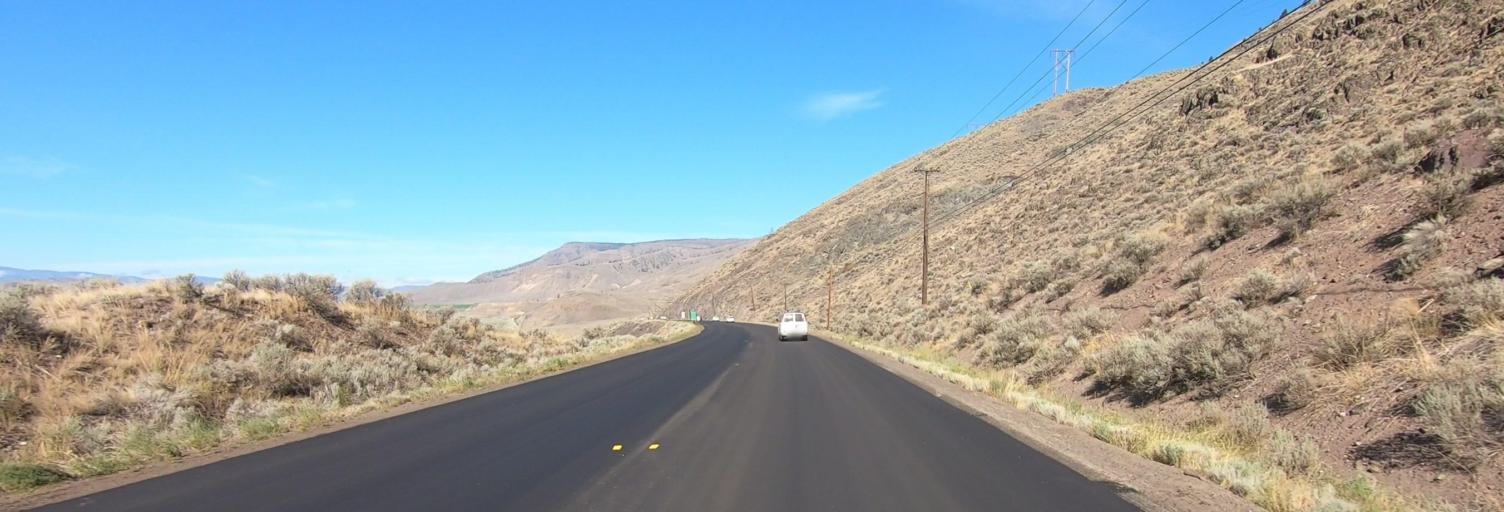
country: CA
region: British Columbia
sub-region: Thompson-Nicola Regional District
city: Ashcroft
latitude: 50.7897
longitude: -121.0764
